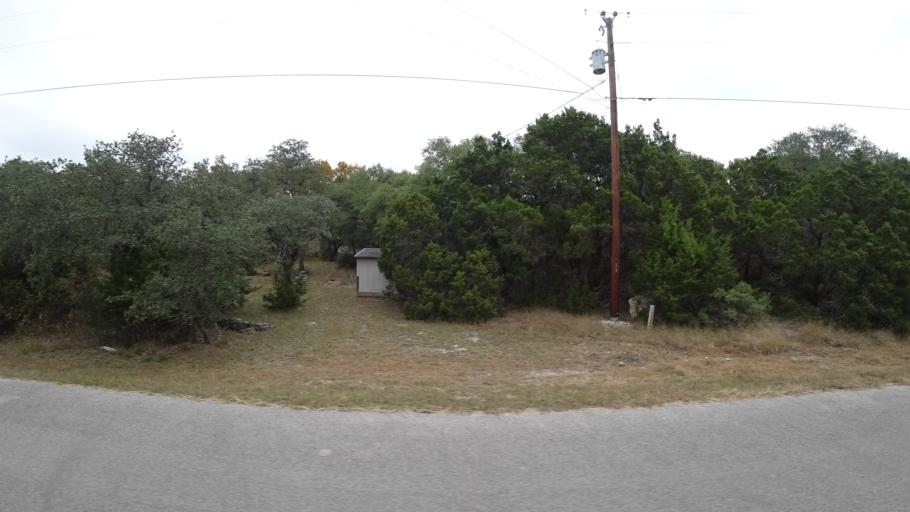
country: US
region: Texas
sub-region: Williamson County
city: Anderson Mill
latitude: 30.4505
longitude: -97.8393
